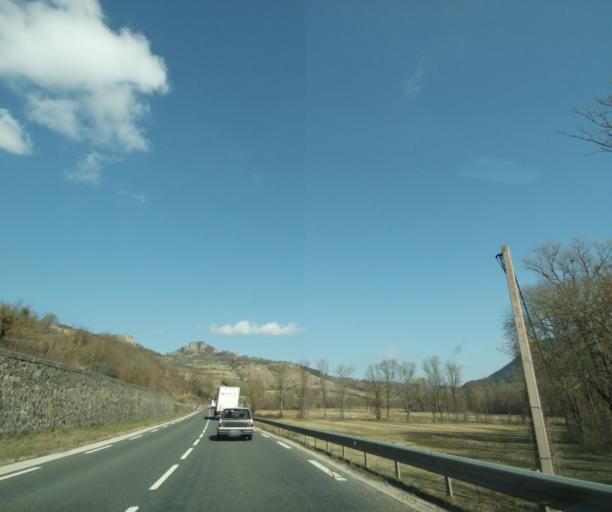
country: FR
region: Languedoc-Roussillon
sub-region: Departement de la Lozere
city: Chanac
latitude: 44.4952
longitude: 3.3960
